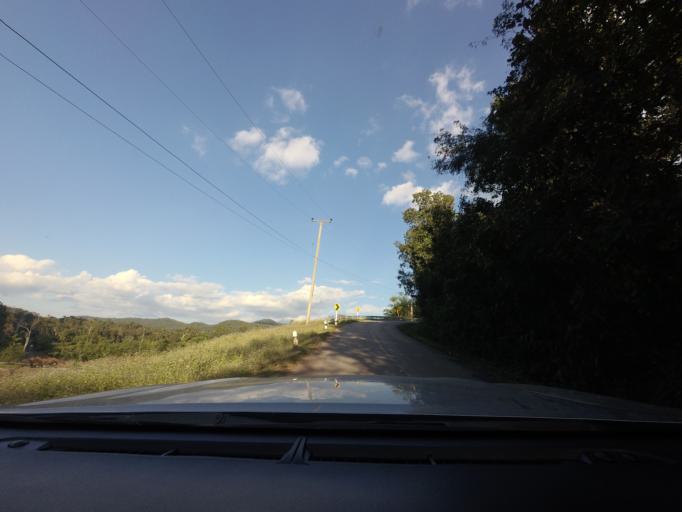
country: TH
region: Chiang Mai
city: Phrao
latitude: 19.5291
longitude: 99.1589
